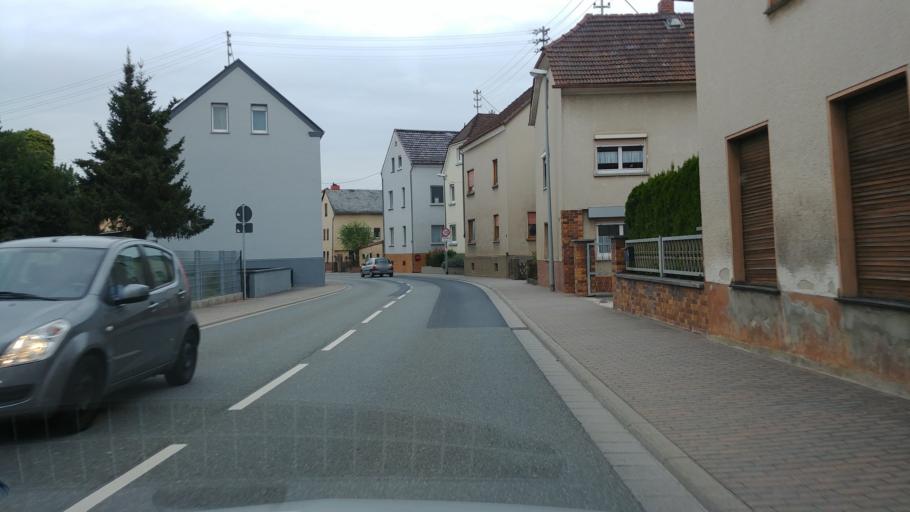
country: DE
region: Rheinland-Pfalz
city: Holzheim
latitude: 50.3441
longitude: 8.0494
